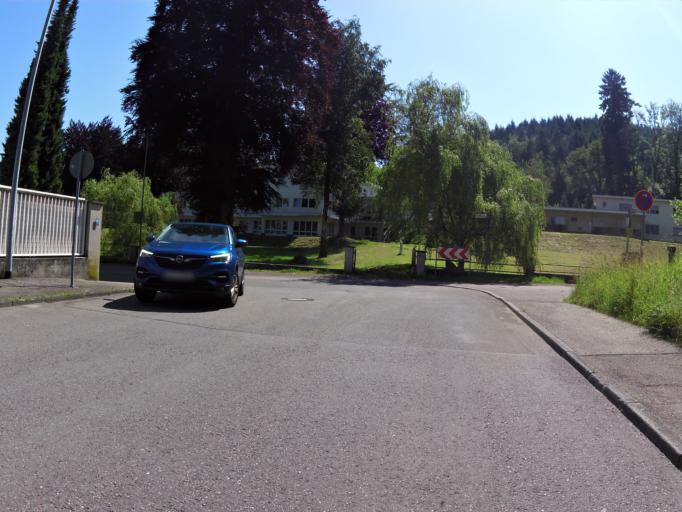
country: DE
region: Baden-Wuerttemberg
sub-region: Freiburg Region
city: Hohberg
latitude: 48.3364
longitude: 7.8922
